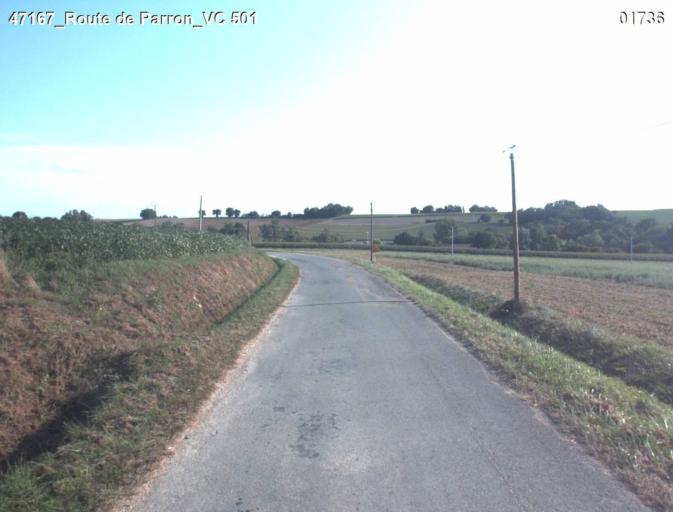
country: FR
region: Aquitaine
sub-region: Departement du Lot-et-Garonne
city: Mezin
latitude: 44.0501
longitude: 0.2632
